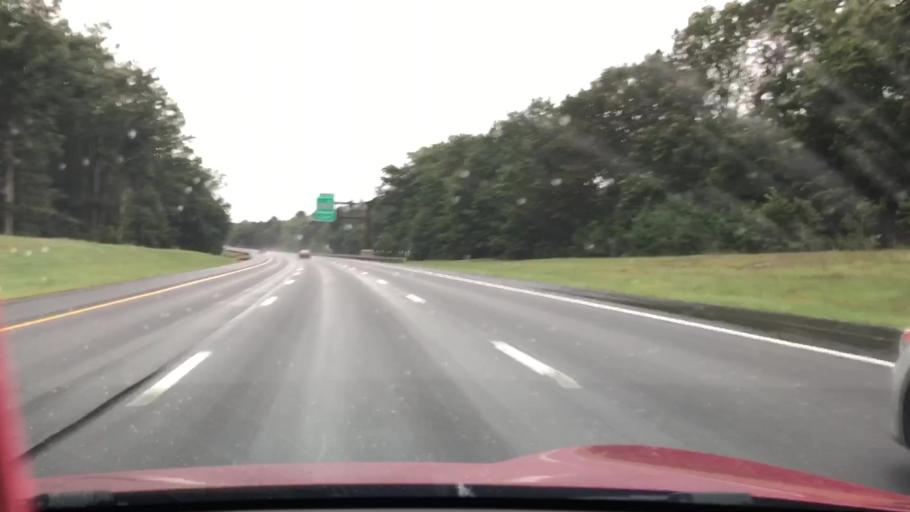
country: US
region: New Jersey
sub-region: Atlantic County
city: Port Republic
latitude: 39.5198
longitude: -74.5172
